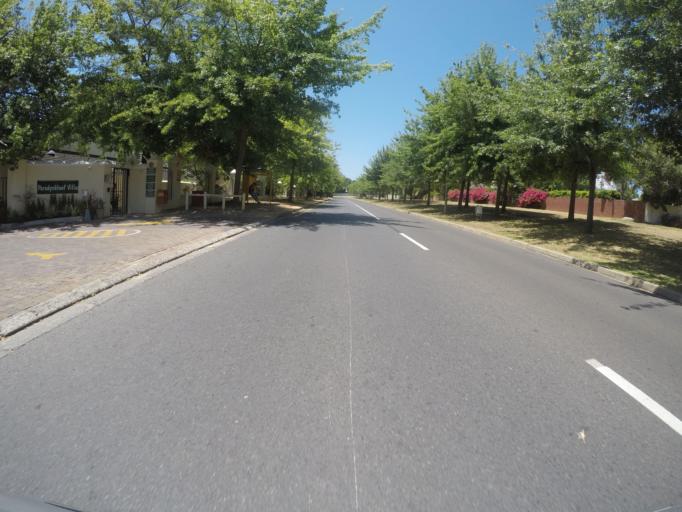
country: ZA
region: Western Cape
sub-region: Cape Winelands District Municipality
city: Stellenbosch
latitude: -33.9639
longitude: 18.8584
